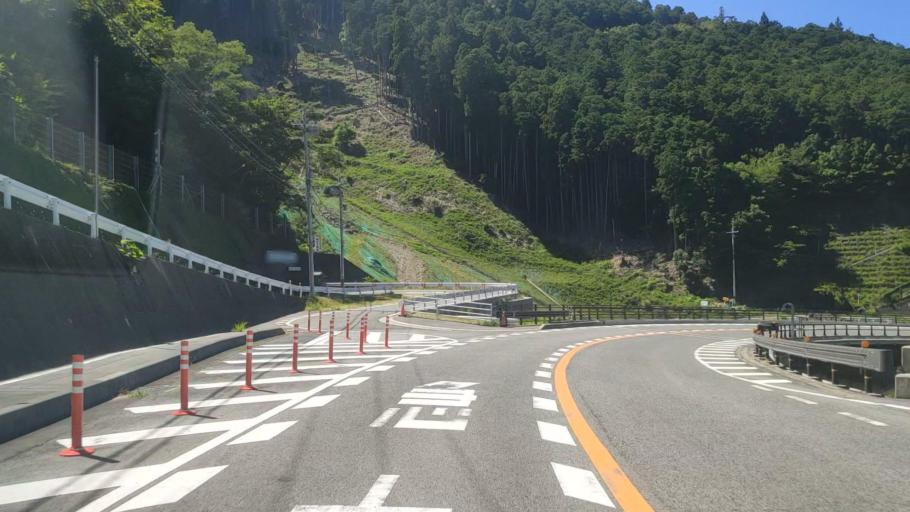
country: JP
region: Nara
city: Yoshino-cho
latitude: 34.3402
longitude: 135.9520
